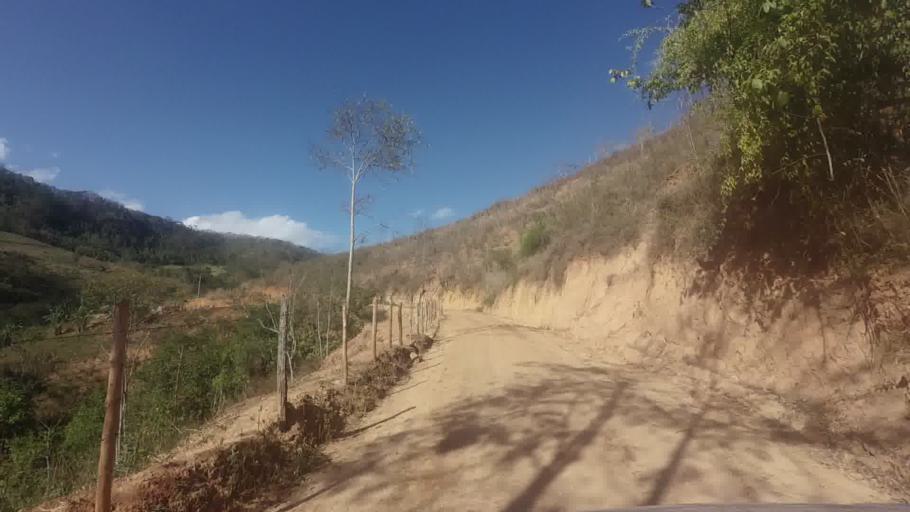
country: BR
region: Espirito Santo
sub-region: Sao Jose Do Calcado
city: Sao Jose do Calcado
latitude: -21.0338
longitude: -41.5966
